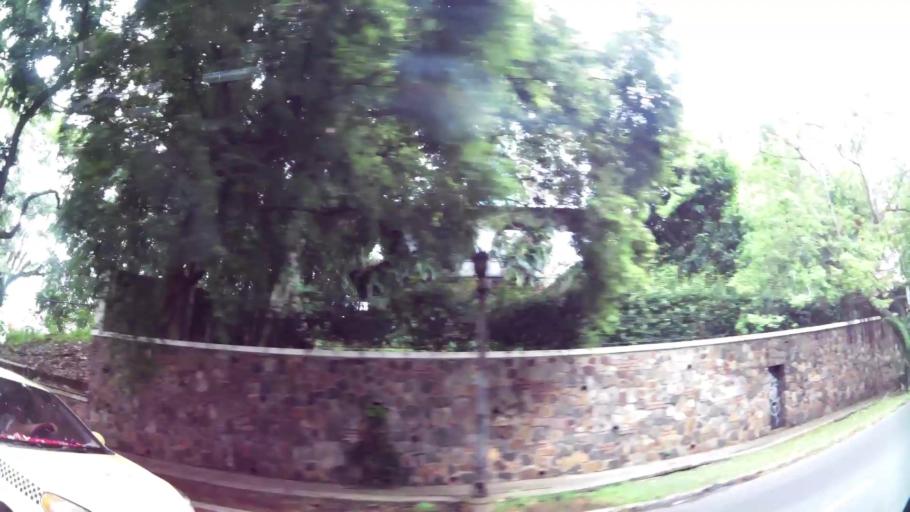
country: PA
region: Panama
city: Panama
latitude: 8.9787
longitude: -79.5283
